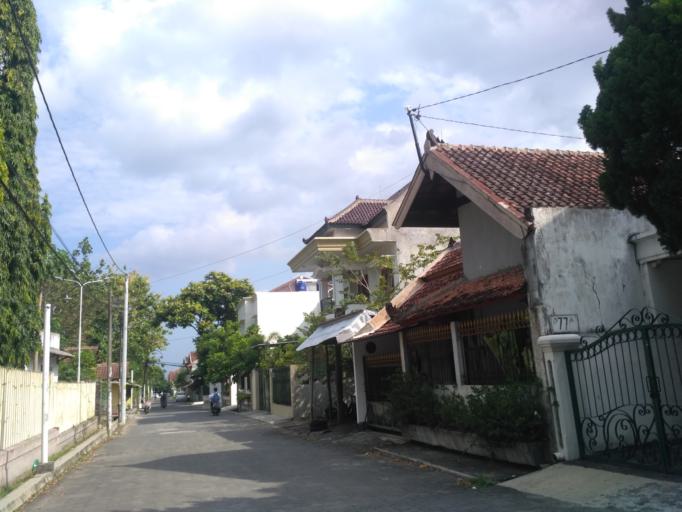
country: ID
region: Daerah Istimewa Yogyakarta
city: Depok
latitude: -7.7784
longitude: 110.4115
